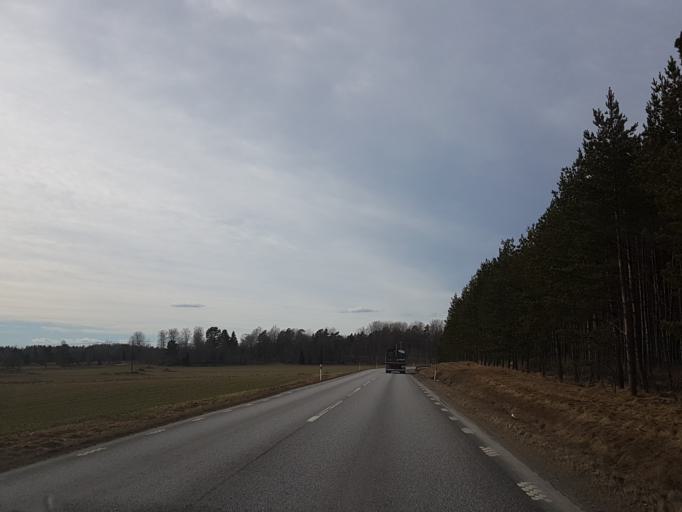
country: SE
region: Stockholm
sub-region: Norrtalje Kommun
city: Norrtalje
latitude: 59.6877
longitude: 18.6698
